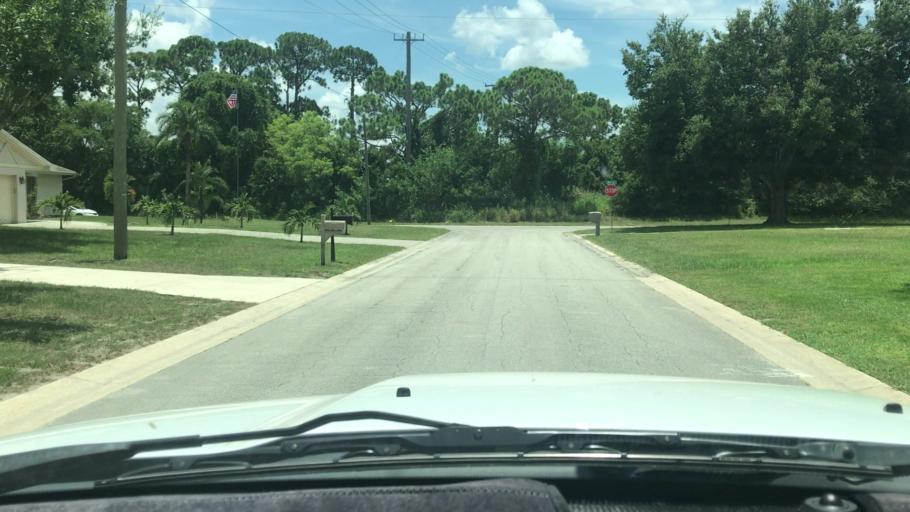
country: US
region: Florida
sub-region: Saint Lucie County
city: Lakewood Park
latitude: 27.5585
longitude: -80.3899
